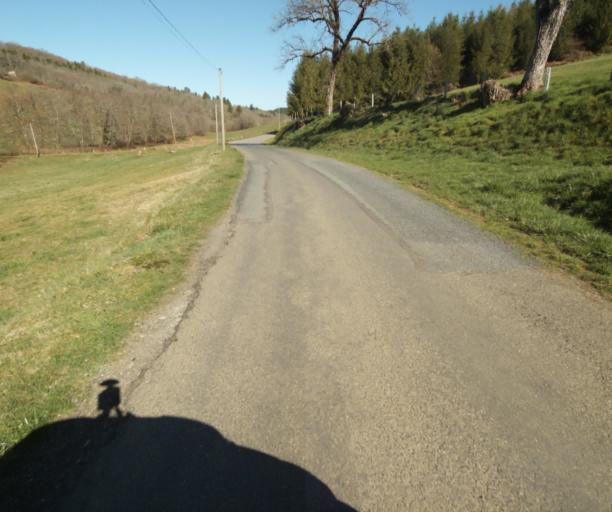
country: FR
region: Limousin
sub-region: Departement de la Correze
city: Seilhac
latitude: 45.3790
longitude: 1.7506
